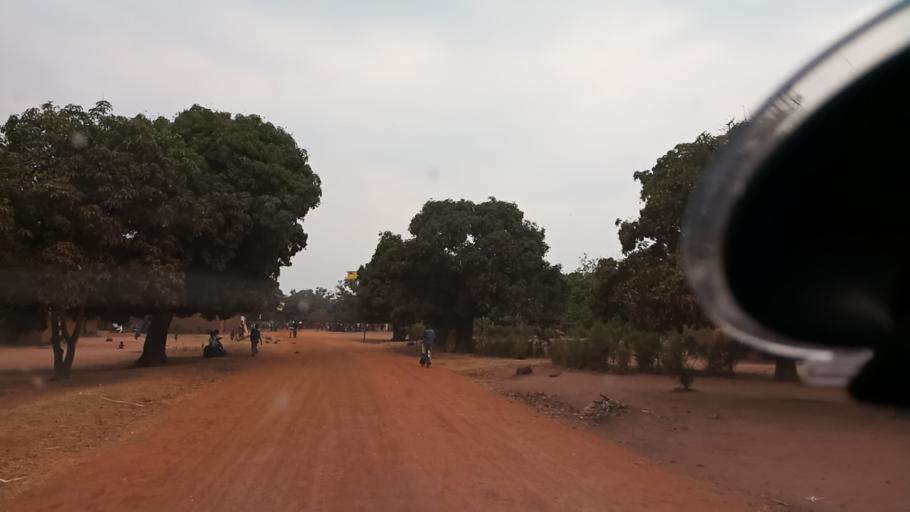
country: ZM
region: Luapula
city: Nchelenge
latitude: -9.1842
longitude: 28.2830
